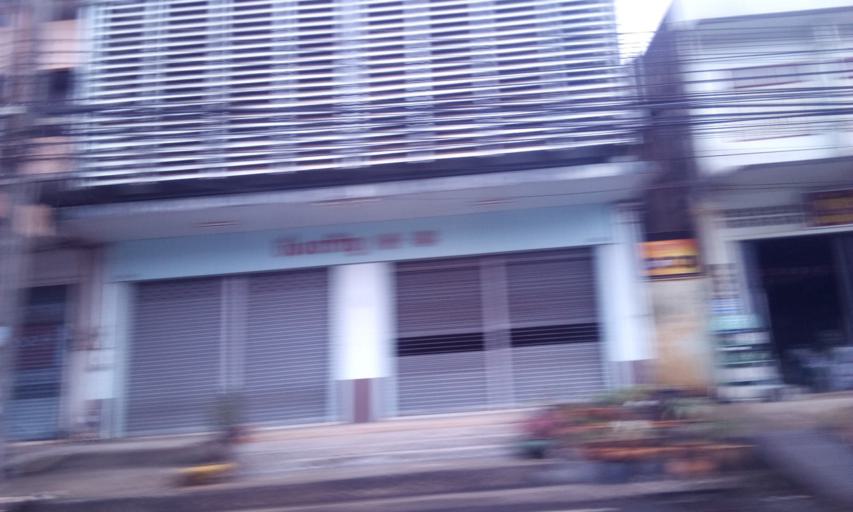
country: TH
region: Chanthaburi
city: Khlung
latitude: 12.4604
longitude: 102.2293
